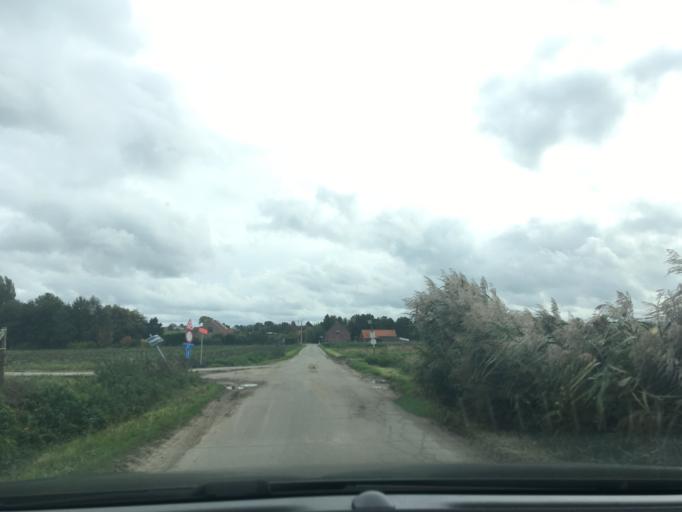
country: BE
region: Flanders
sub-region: Provincie West-Vlaanderen
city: Moorslede
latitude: 50.9050
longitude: 3.0512
